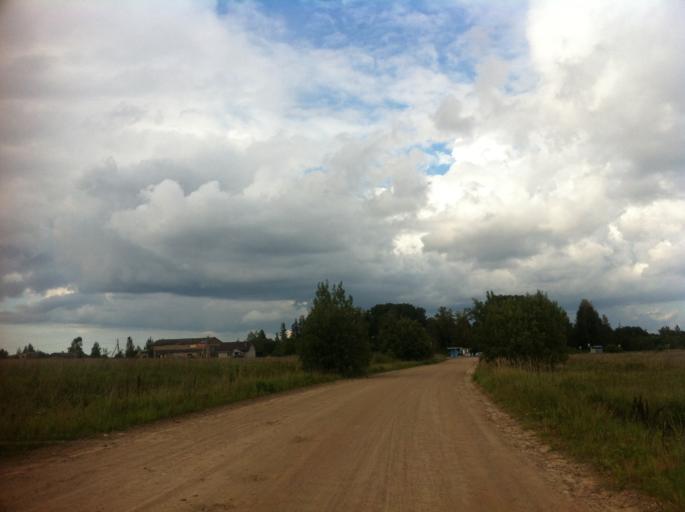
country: RU
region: Pskov
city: Izborsk
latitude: 57.8358
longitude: 27.9863
